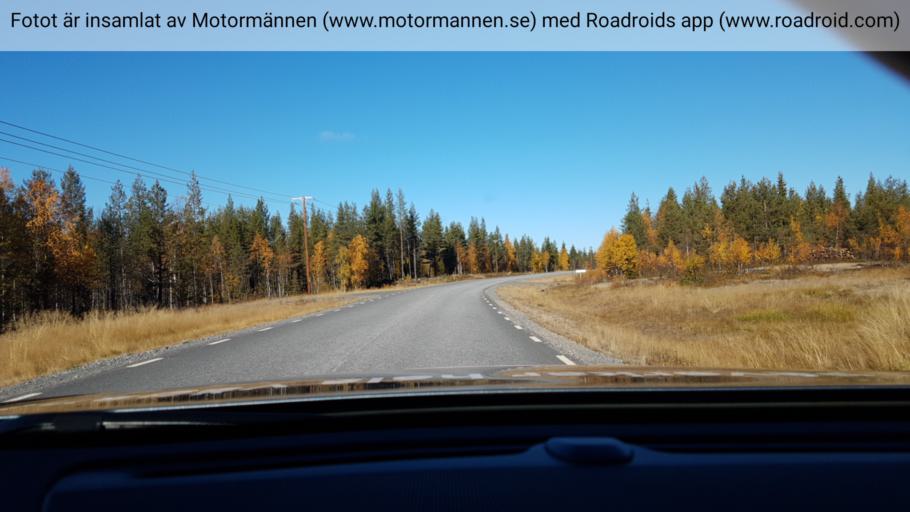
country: SE
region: Norrbotten
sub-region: Gallivare Kommun
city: Gaellivare
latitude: 66.8146
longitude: 21.0429
